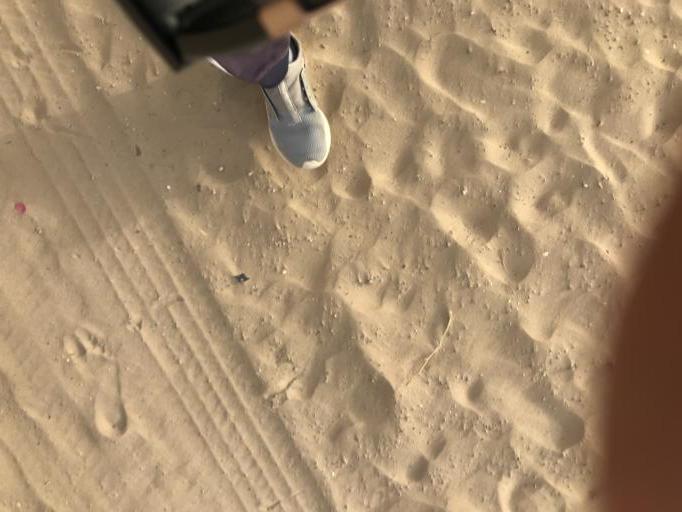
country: SN
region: Saint-Louis
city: Saint-Louis
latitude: 16.0363
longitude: -16.4455
